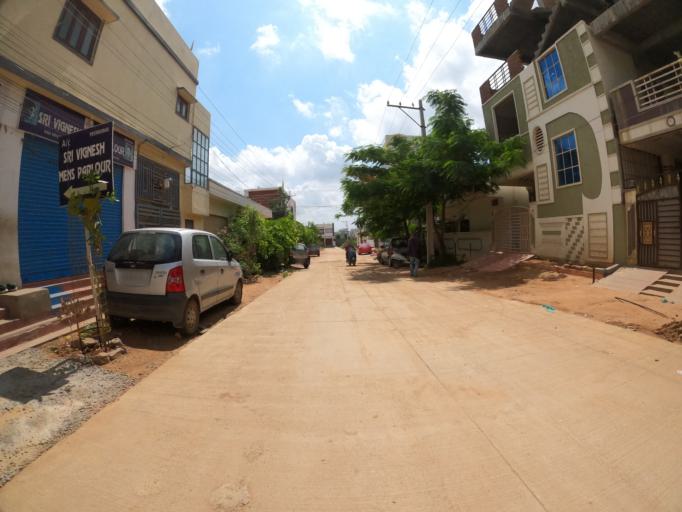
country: IN
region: Telangana
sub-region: Hyderabad
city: Hyderabad
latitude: 17.3612
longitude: 78.3811
